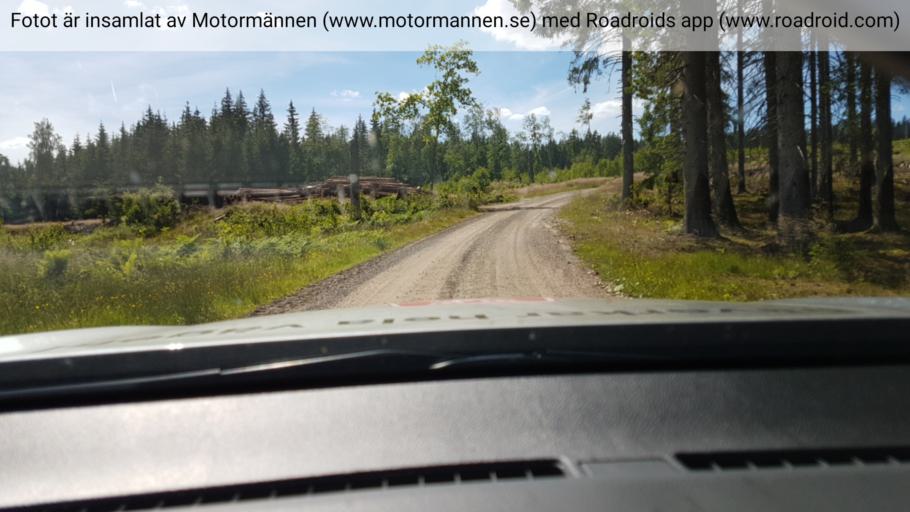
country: SE
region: Joenkoeping
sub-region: Vaggeryds Kommun
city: Skillingaryd
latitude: 57.3566
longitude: 14.0685
